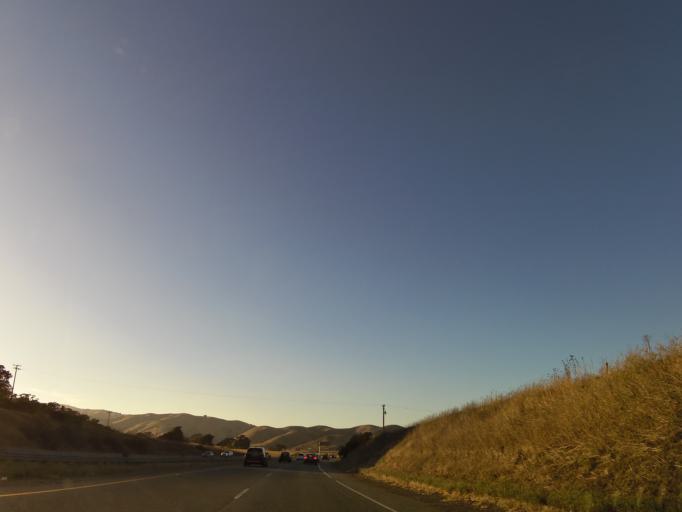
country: US
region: California
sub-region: Santa Clara County
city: Gilroy
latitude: 36.9344
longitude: -121.5517
